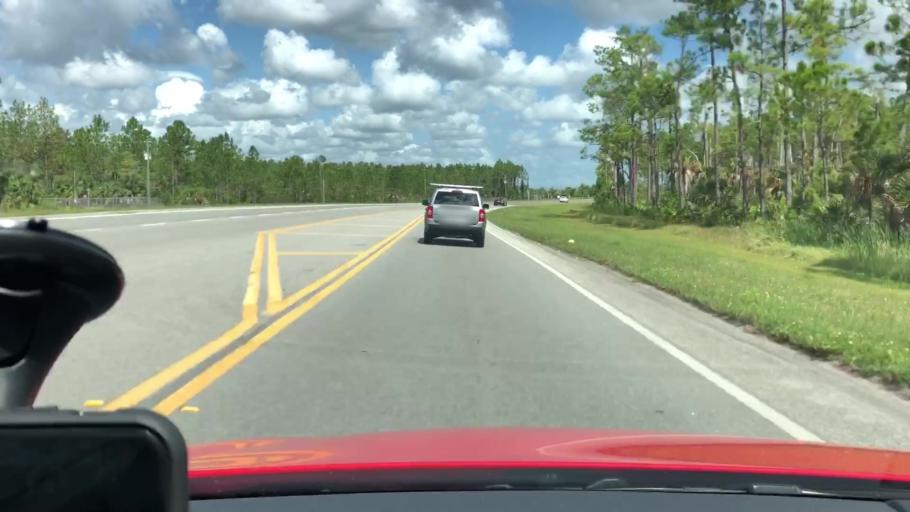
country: US
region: Florida
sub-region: Volusia County
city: Holly Hill
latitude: 29.2092
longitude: -81.1198
